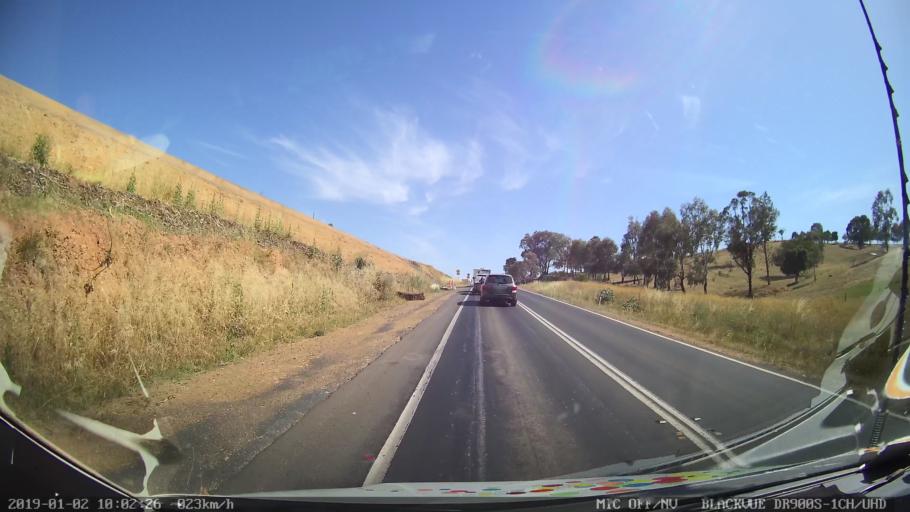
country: AU
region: New South Wales
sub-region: Gundagai
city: Gundagai
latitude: -35.1830
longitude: 148.1264
